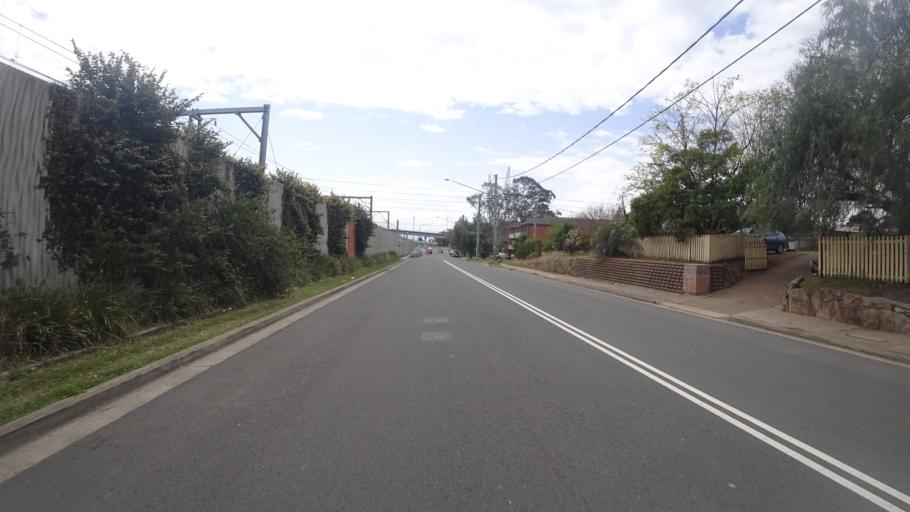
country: AU
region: New South Wales
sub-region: Campbelltown Municipality
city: Glenfield
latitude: -33.9681
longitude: 150.8981
